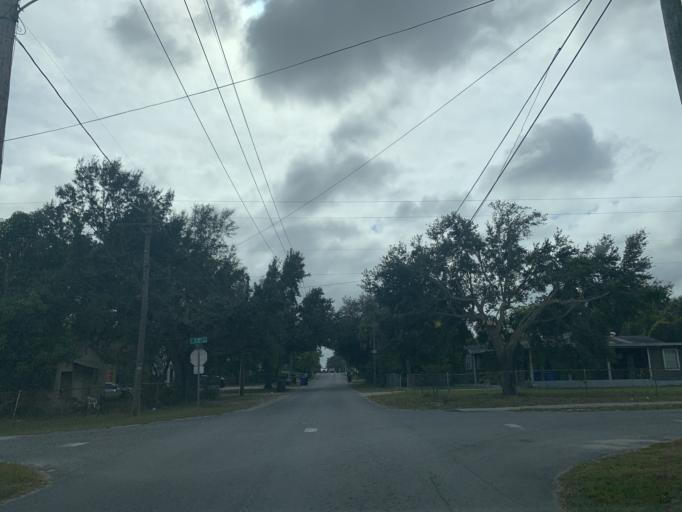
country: US
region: Florida
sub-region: Hillsborough County
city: East Lake-Orient Park
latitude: 27.9797
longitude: -82.3937
